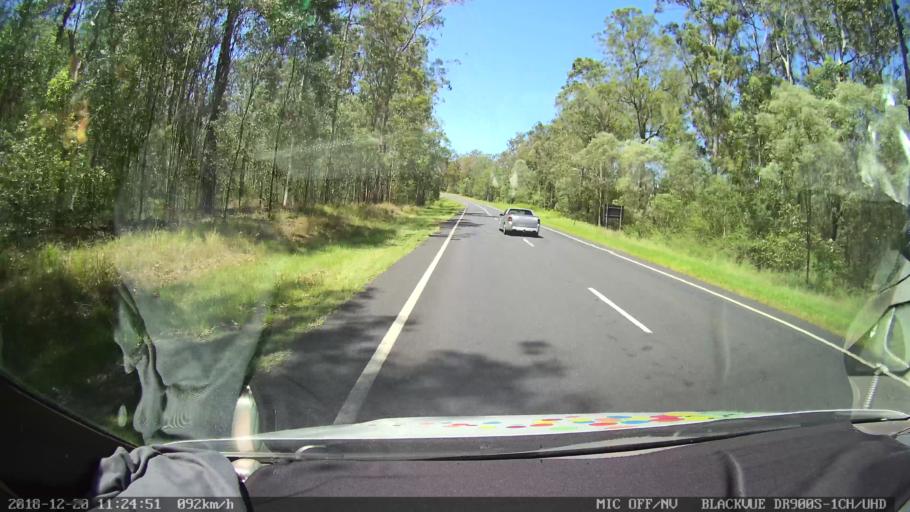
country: AU
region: New South Wales
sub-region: Richmond Valley
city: Casino
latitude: -29.0798
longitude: 153.0007
